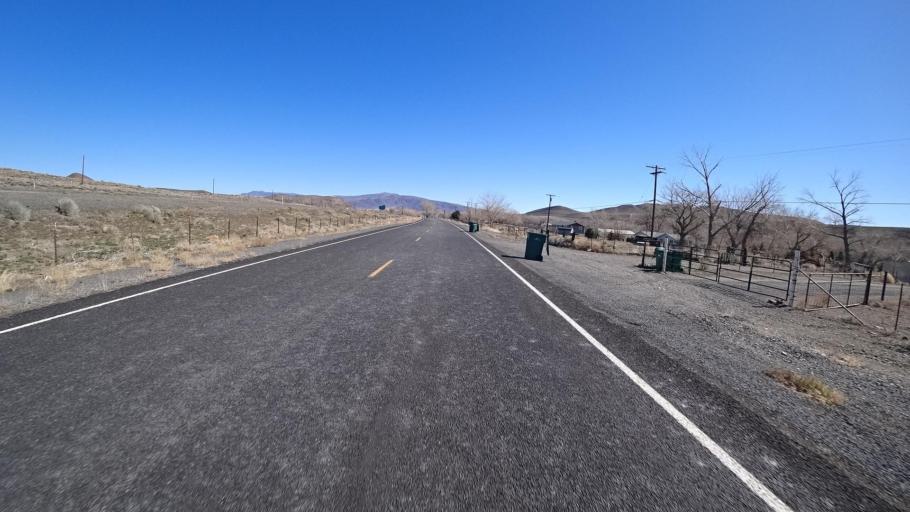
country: US
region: Nevada
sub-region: Lyon County
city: Fernley
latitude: 39.6061
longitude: -119.3247
